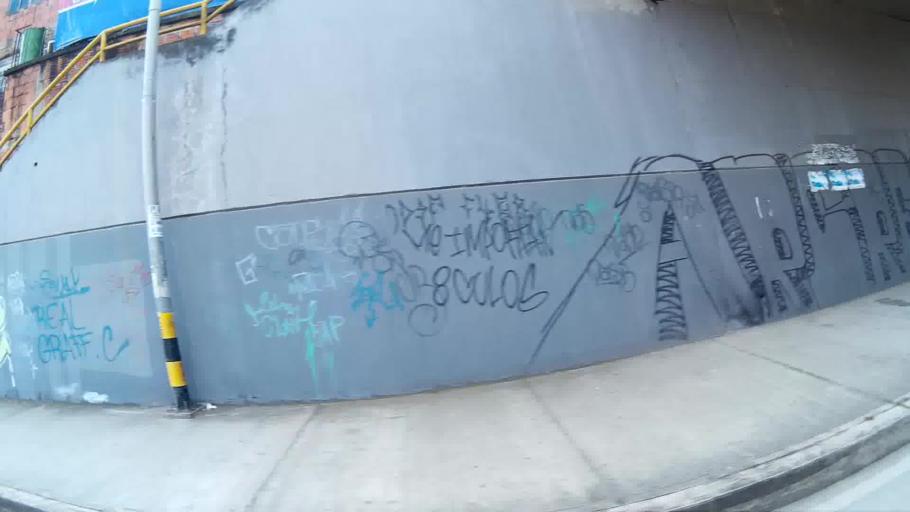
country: CO
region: Risaralda
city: Pereira
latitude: 4.8059
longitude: -75.7347
